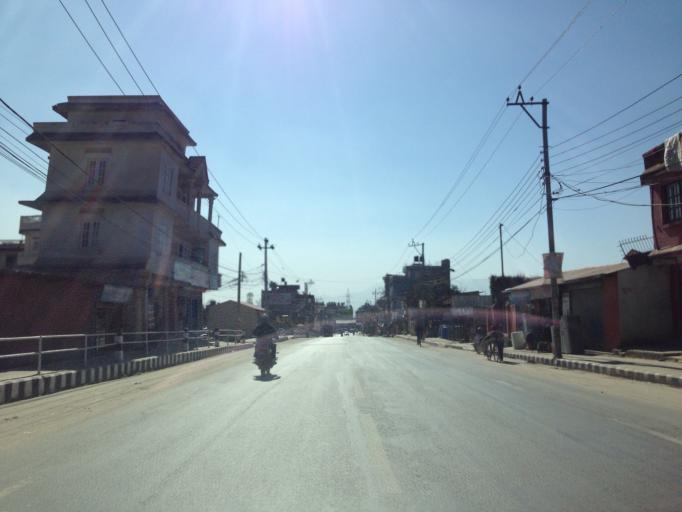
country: NP
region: Central Region
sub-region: Bagmati Zone
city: Kathmandu
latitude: 27.7704
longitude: 85.3580
